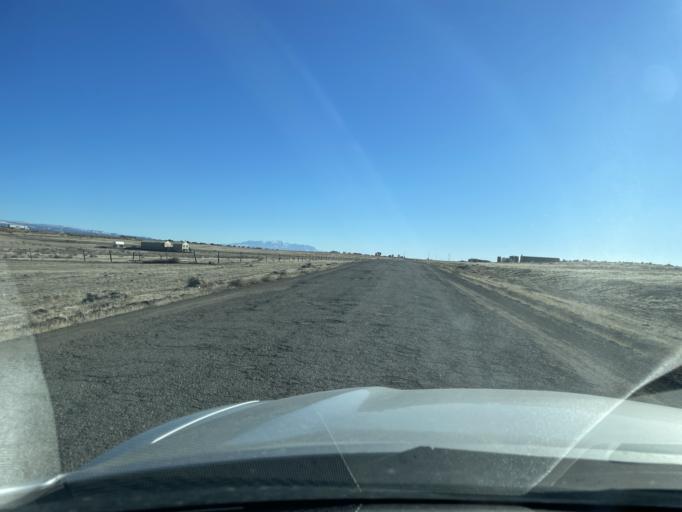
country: US
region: Colorado
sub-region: Mesa County
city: Loma
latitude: 39.1794
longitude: -109.1307
